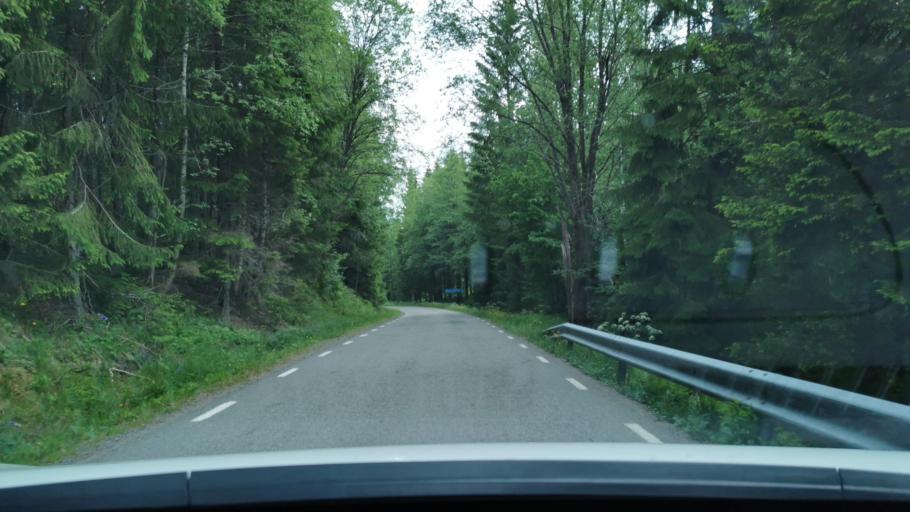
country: SE
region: Vaestra Goetaland
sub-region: Bengtsfors Kommun
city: Dals Langed
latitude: 58.8145
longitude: 12.3261
